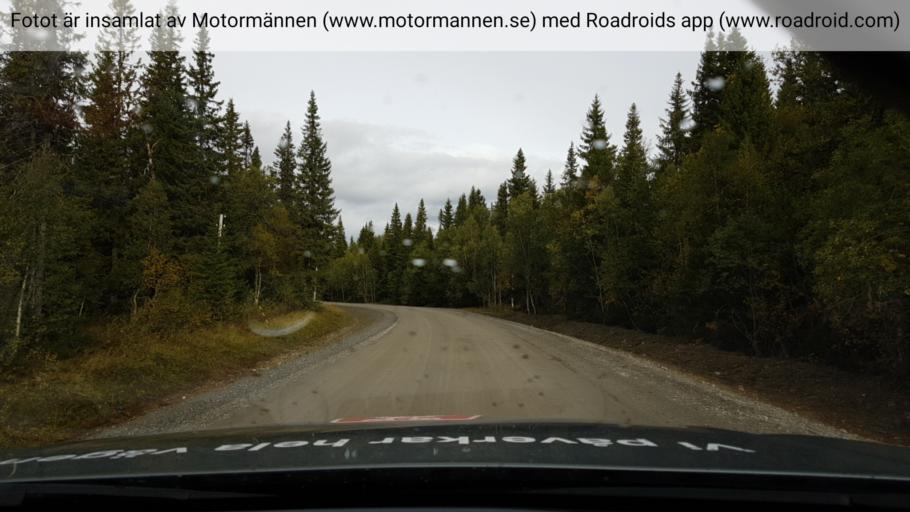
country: NO
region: Nord-Trondelag
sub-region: Snasa
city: Snaase
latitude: 63.7256
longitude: 12.4762
